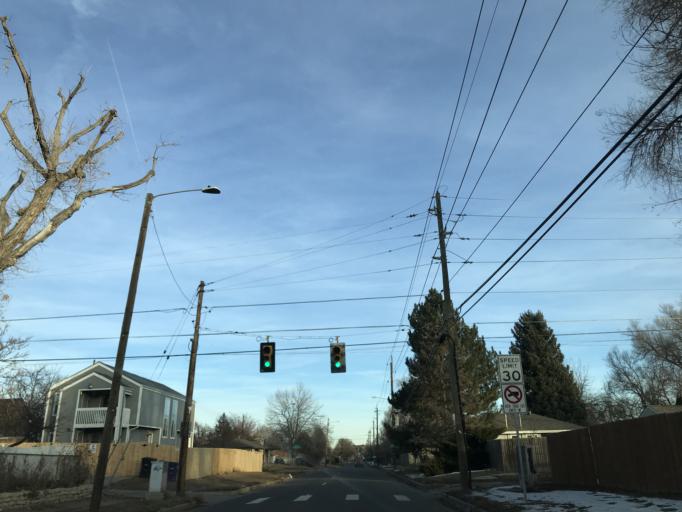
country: US
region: Colorado
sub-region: Arapahoe County
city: Glendale
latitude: 39.7387
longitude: -104.8926
